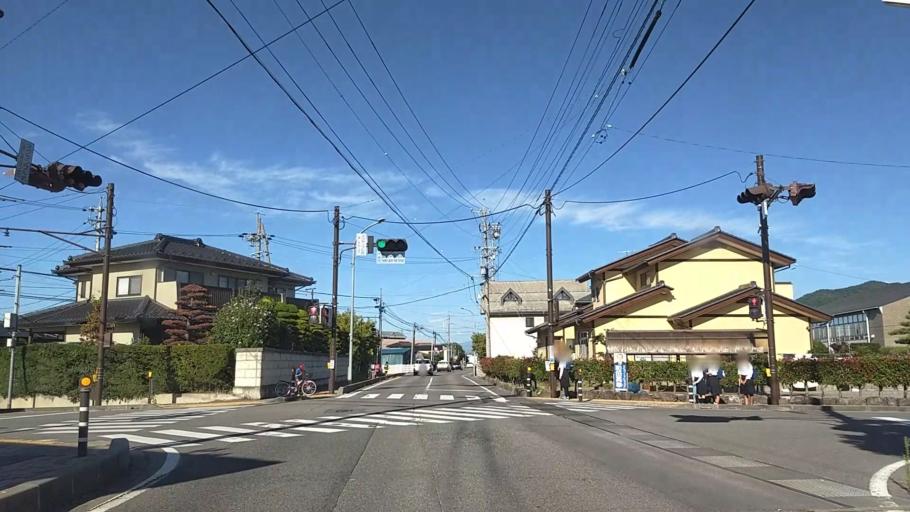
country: JP
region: Nagano
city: Nagano-shi
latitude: 36.5421
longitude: 138.1312
